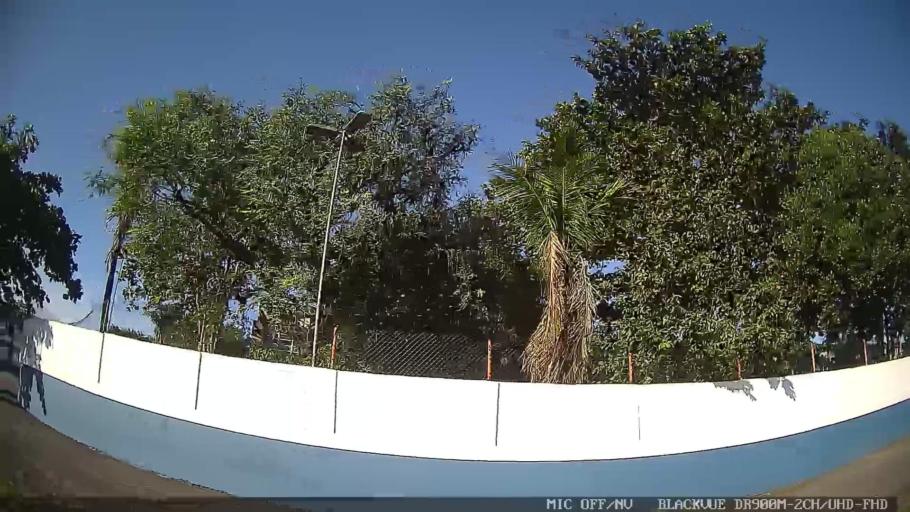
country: BR
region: Sao Paulo
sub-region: Guaruja
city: Guaruja
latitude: -23.9594
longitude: -46.2798
